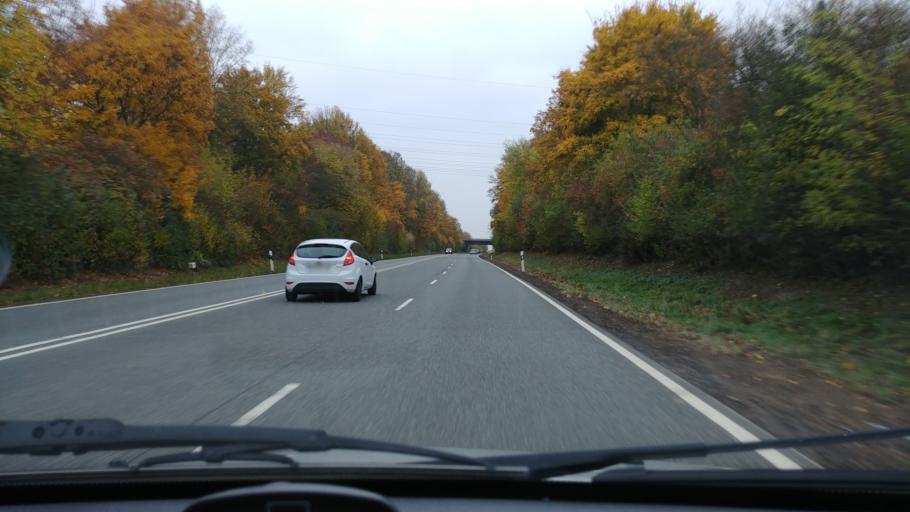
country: DE
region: Hesse
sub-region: Regierungsbezirk Giessen
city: Dehrn
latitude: 50.4467
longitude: 8.0901
